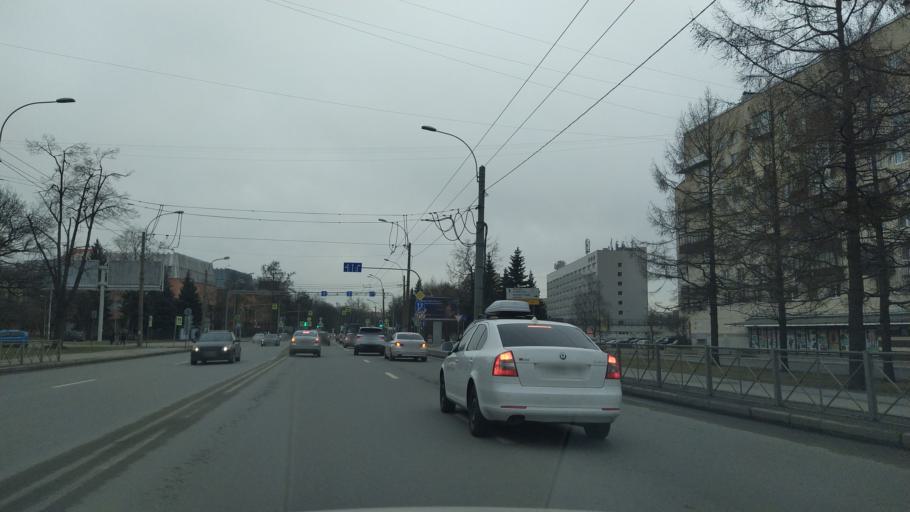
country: RU
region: St.-Petersburg
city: Sosnovka
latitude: 60.0075
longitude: 30.3528
